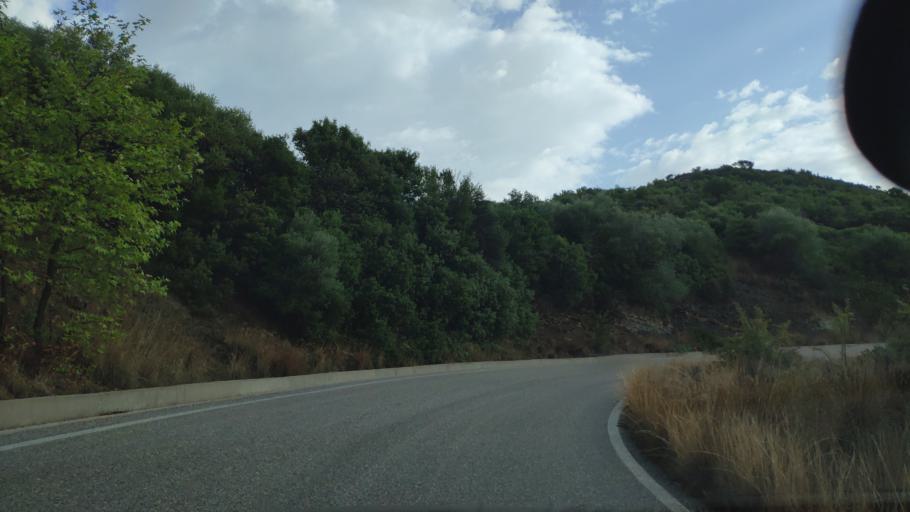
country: GR
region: West Greece
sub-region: Nomos Aitolias kai Akarnanias
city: Sardinia
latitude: 38.8889
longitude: 21.2368
